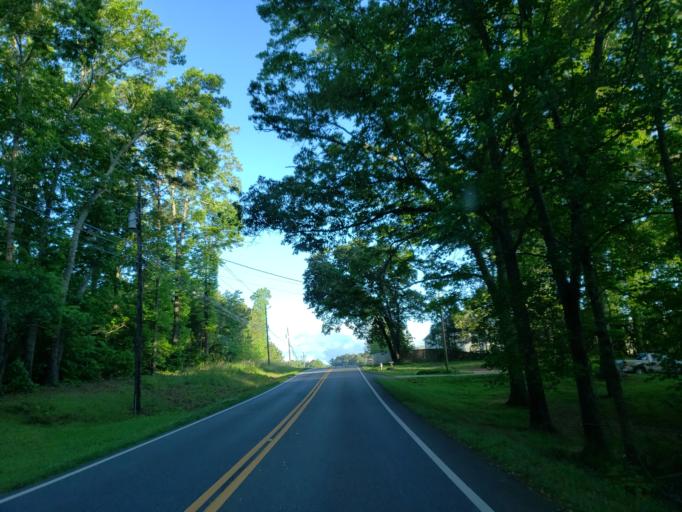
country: US
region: Georgia
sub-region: Cherokee County
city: Holly Springs
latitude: 34.2078
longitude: -84.5249
